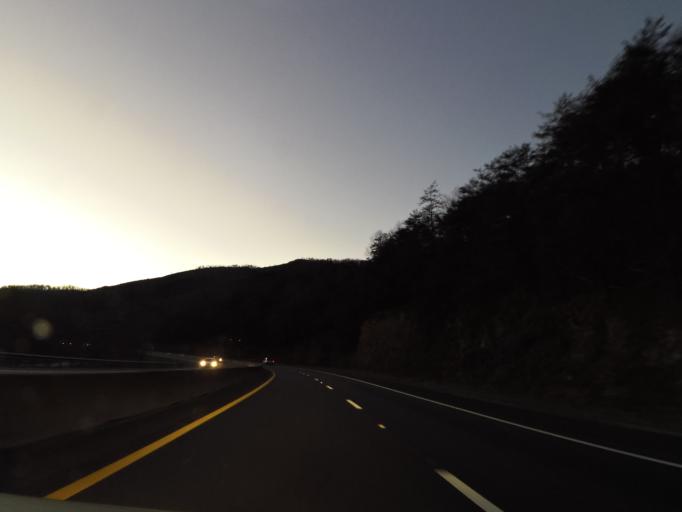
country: US
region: Tennessee
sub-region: Cocke County
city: Newport
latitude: 35.8213
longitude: -83.1514
